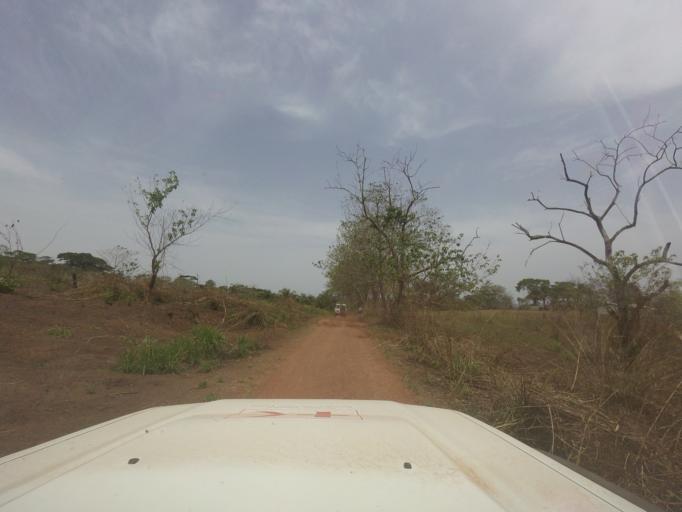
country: SL
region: Eastern Province
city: Buedu
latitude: 8.4756
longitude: -10.3357
